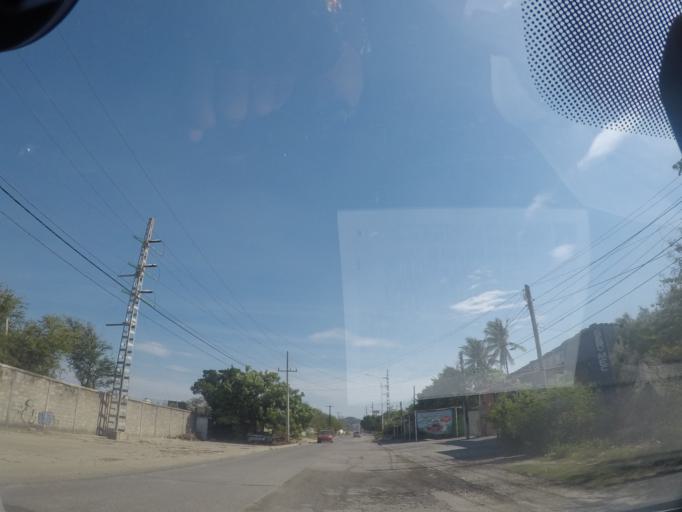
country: MX
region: Oaxaca
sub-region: Salina Cruz
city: Salina Cruz
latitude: 16.2113
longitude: -95.1944
